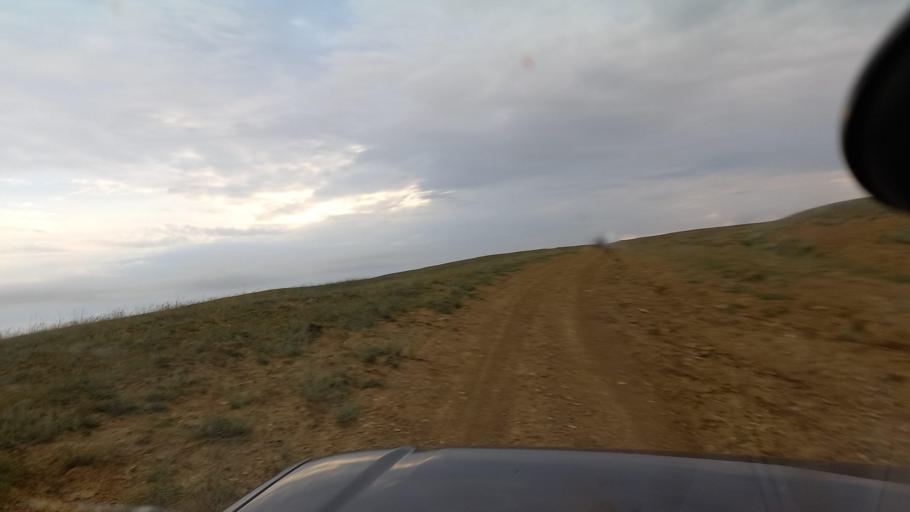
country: RU
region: Krasnodarskiy
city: Taman'
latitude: 45.2008
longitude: 36.7925
